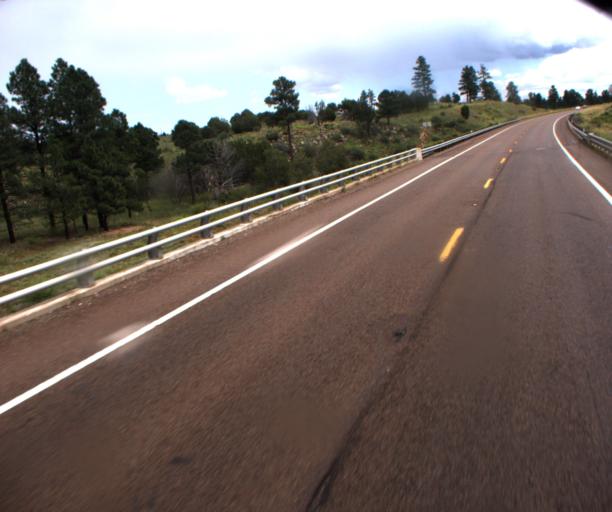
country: US
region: Arizona
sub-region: Navajo County
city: Linden
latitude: 34.3642
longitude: -110.3324
